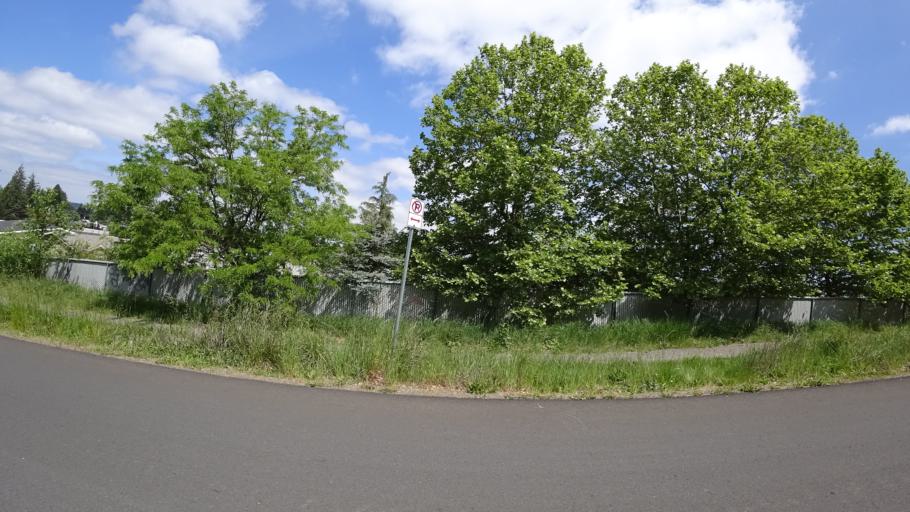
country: US
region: Oregon
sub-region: Clackamas County
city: Happy Valley
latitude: 45.4928
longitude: -122.4958
